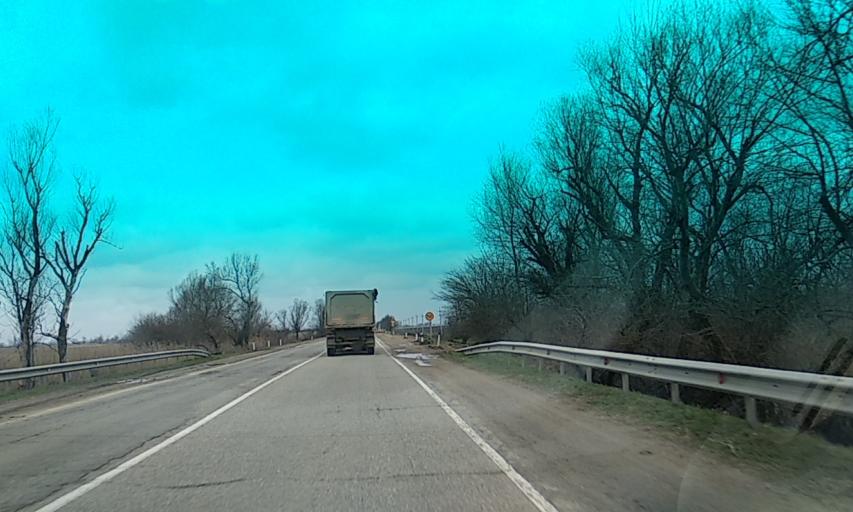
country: RU
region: Adygeya
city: Beloye
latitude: 44.9987
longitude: 39.7087
